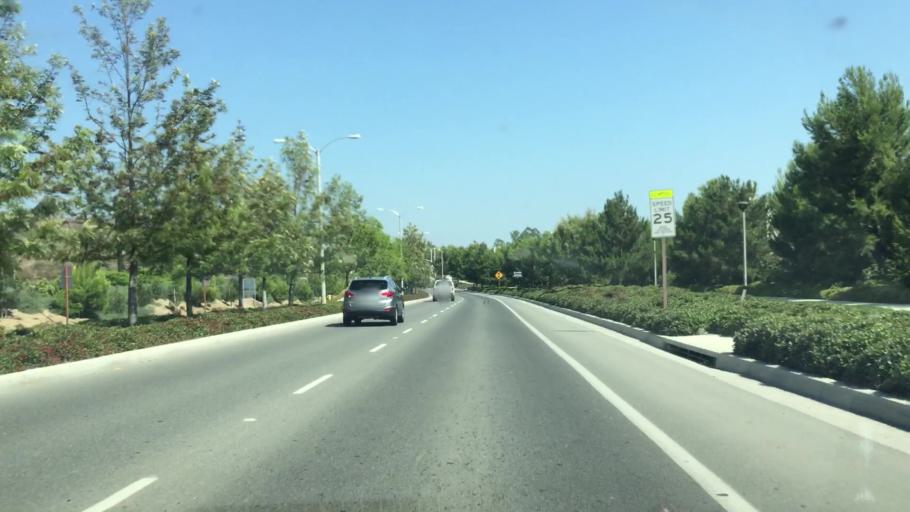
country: US
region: California
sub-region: Orange County
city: Lake Forest
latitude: 33.7088
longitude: -117.7351
